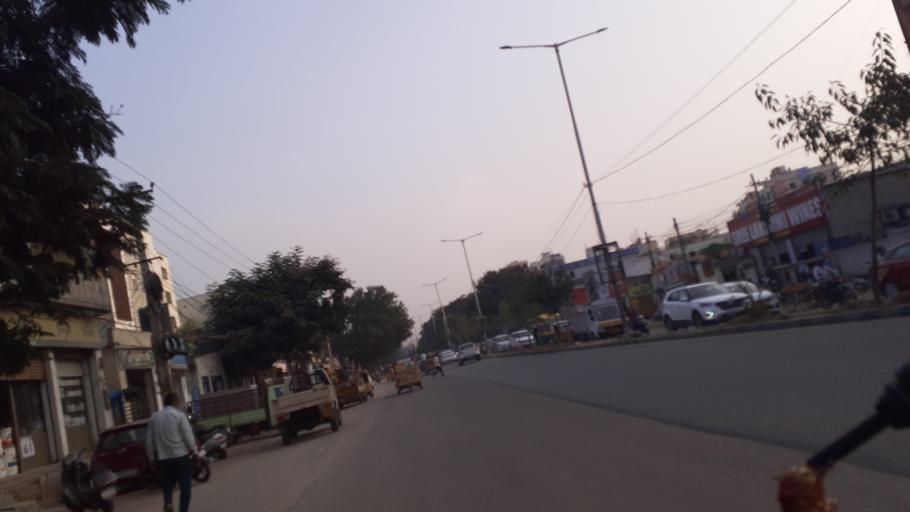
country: IN
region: Telangana
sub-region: Rangareddi
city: Kukatpalli
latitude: 17.4755
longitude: 78.3633
